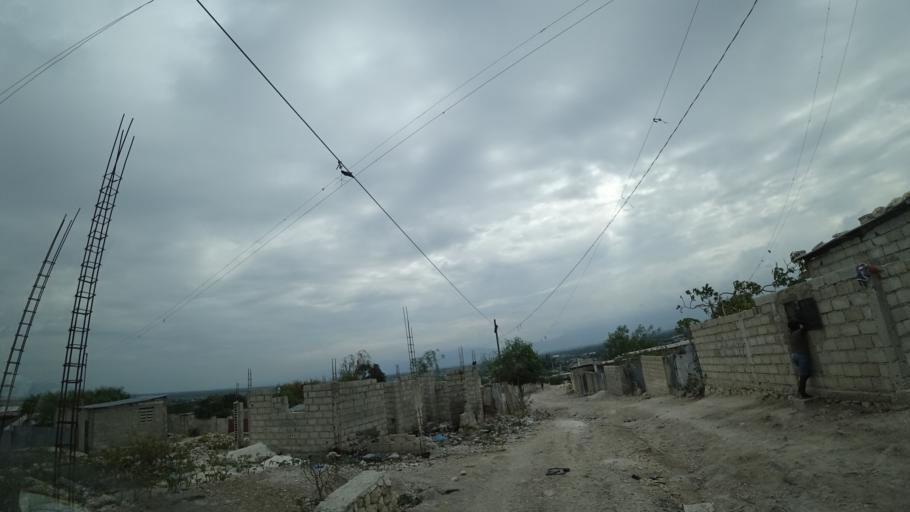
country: HT
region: Ouest
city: Croix des Bouquets
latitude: 18.6544
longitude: -72.2675
